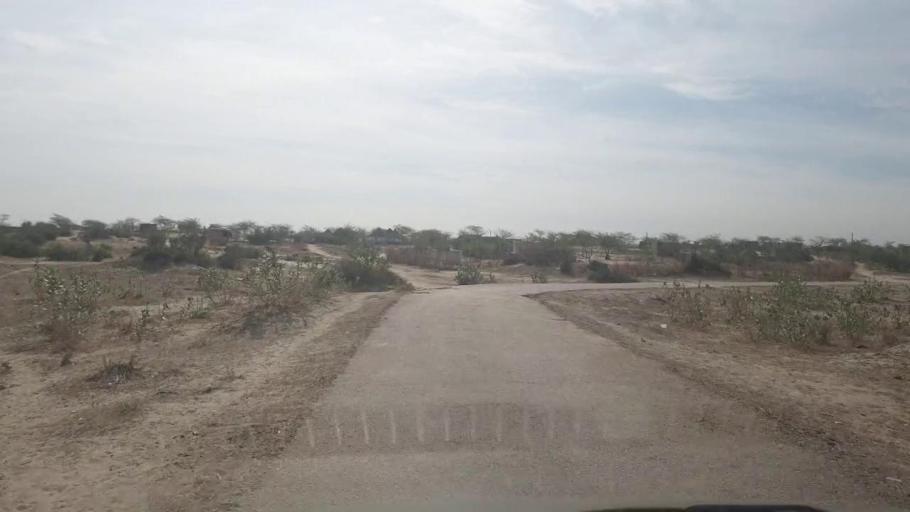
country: PK
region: Sindh
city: Umarkot
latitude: 25.2812
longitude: 69.7452
